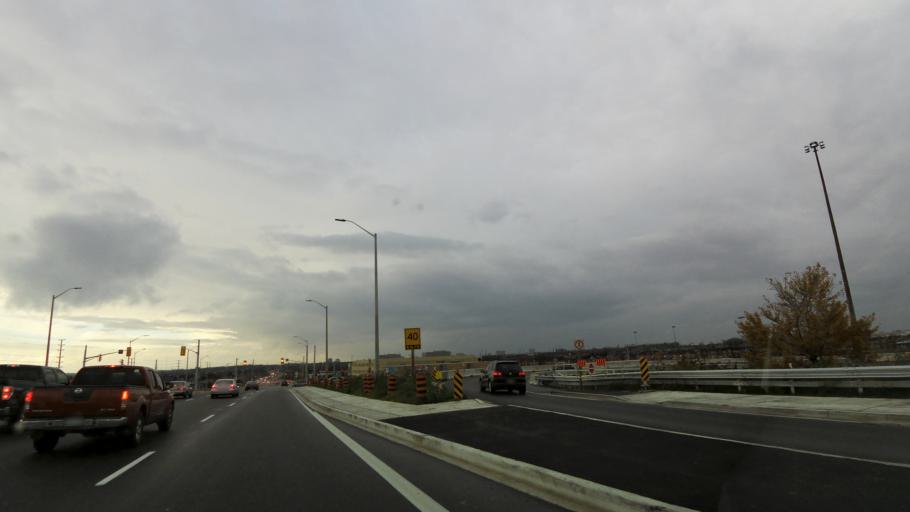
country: CA
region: Ontario
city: Mississauga
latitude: 43.6211
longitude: -79.7084
